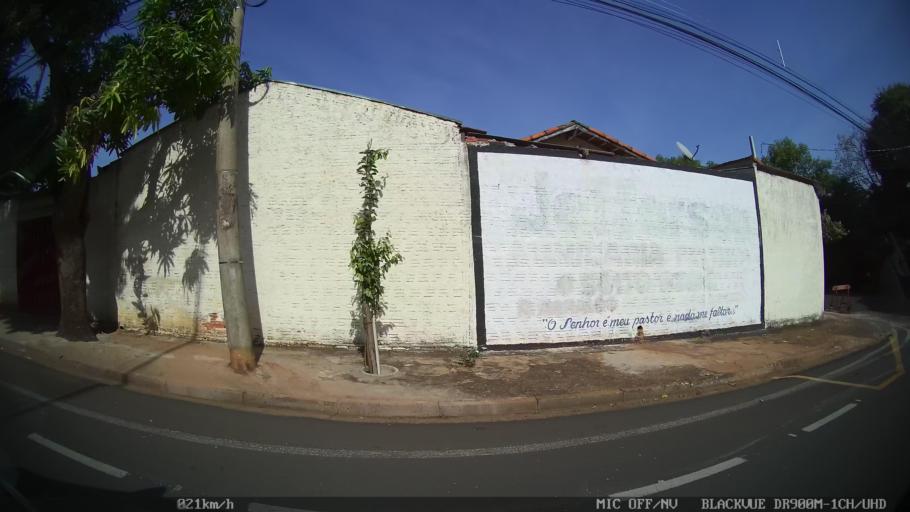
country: BR
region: Sao Paulo
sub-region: Sao Jose Do Rio Preto
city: Sao Jose do Rio Preto
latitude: -20.7957
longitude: -49.4241
